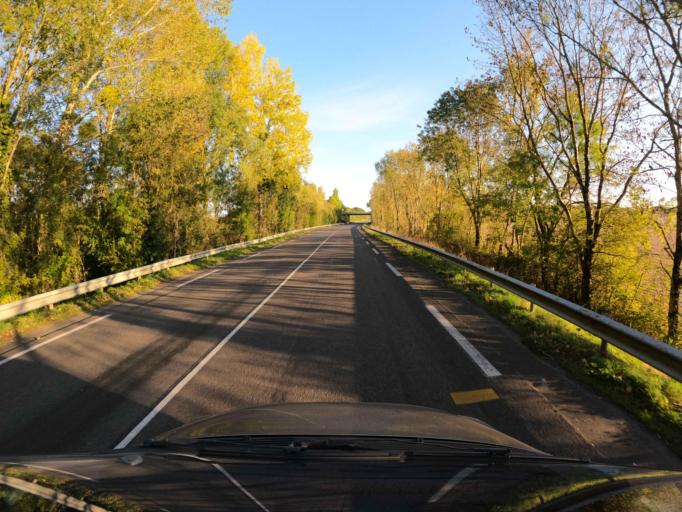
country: FR
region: Pays de la Loire
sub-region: Departement de la Vendee
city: Sainte-Hermine
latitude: 46.5563
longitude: -1.0436
